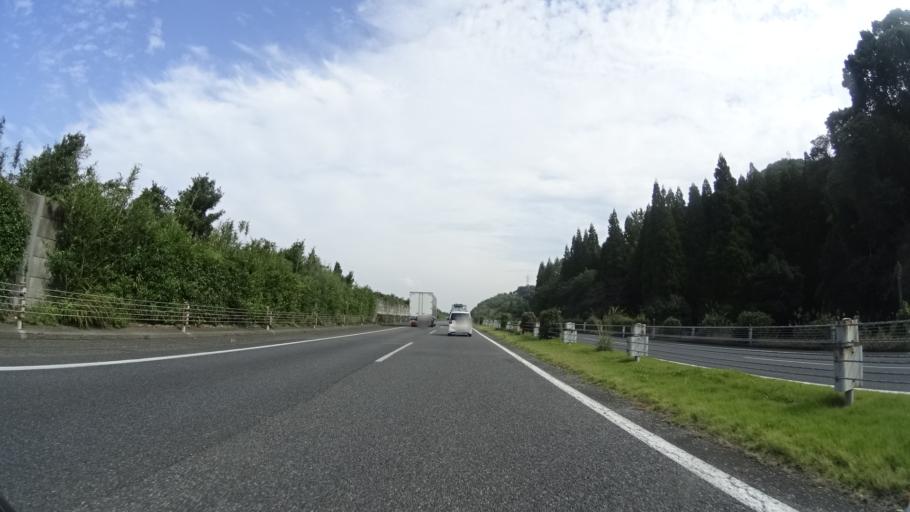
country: JP
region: Kumamoto
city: Yatsushiro
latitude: 32.5260
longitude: 130.6631
